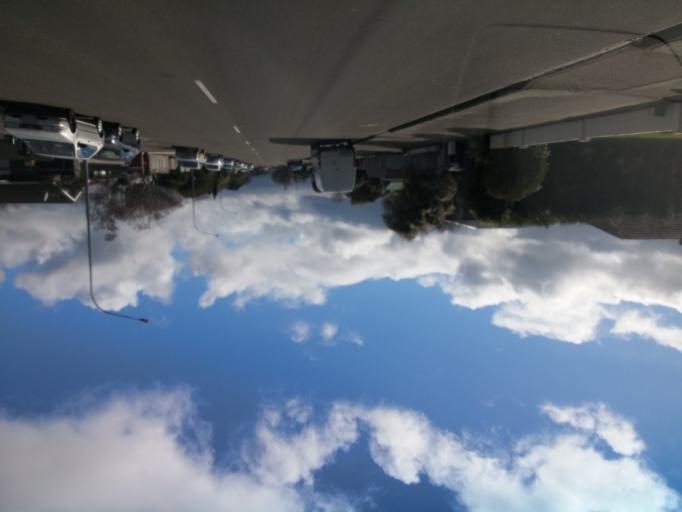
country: NZ
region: Manawatu-Wanganui
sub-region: Palmerston North City
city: Palmerston North
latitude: -40.3659
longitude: 175.5991
